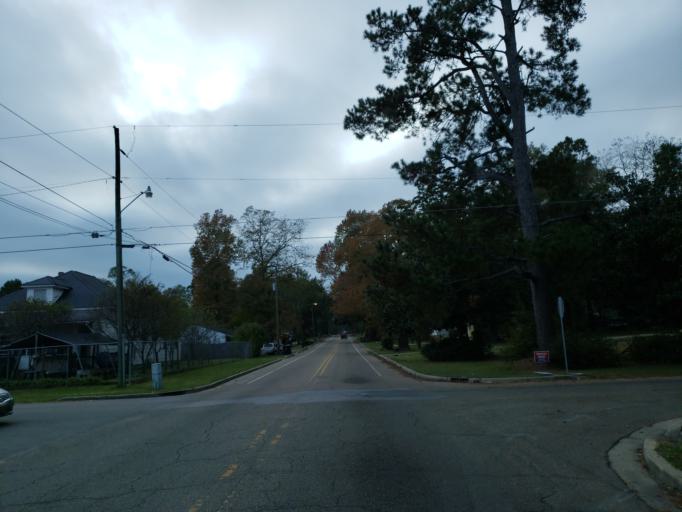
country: US
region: Mississippi
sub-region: Forrest County
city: Hattiesburg
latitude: 31.3175
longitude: -89.2930
